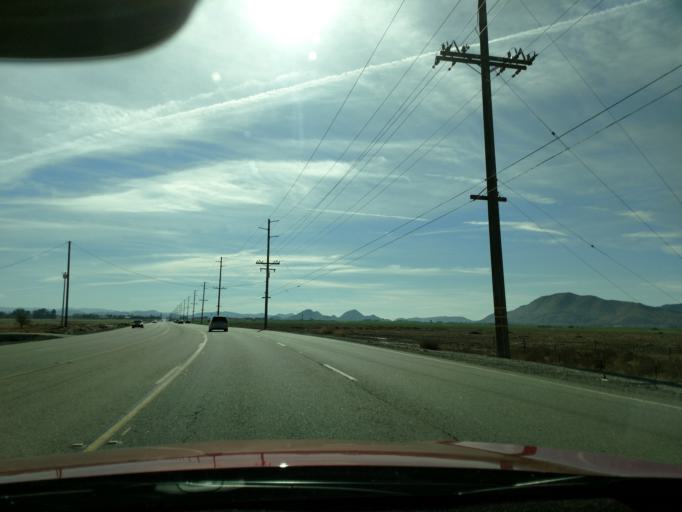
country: US
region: California
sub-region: Riverside County
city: San Jacinto
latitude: 33.8166
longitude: -117.0070
